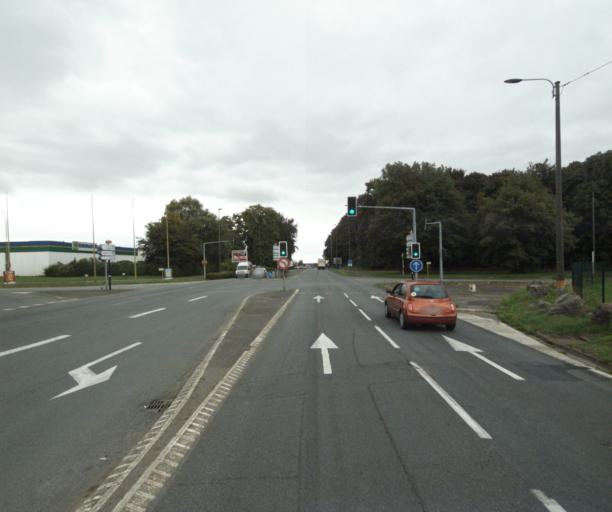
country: FR
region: Nord-Pas-de-Calais
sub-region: Departement du Nord
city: Lesquin
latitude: 50.5813
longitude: 3.1123
